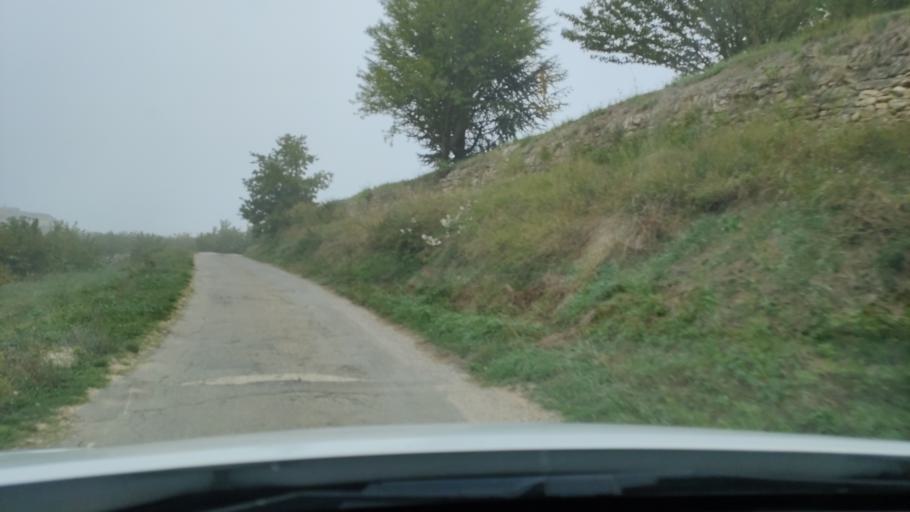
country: FR
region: Provence-Alpes-Cote d'Azur
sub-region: Departement du Vaucluse
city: Bonnieux
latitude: 43.8398
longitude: 5.3215
